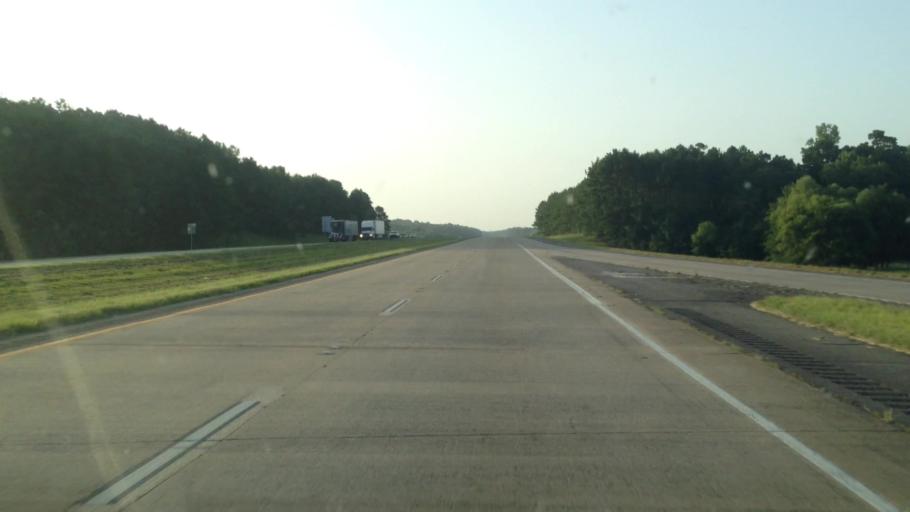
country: US
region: Louisiana
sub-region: Grant Parish
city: Colfax
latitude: 31.4914
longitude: -92.8576
